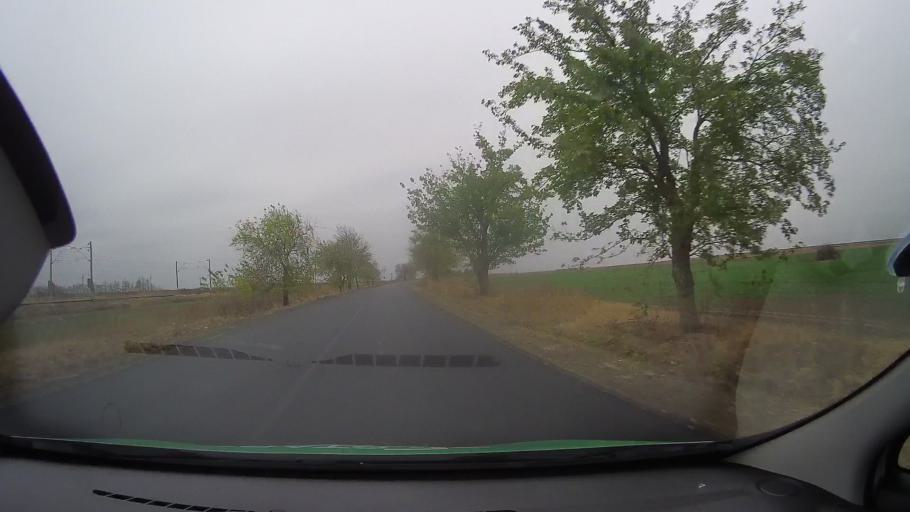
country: RO
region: Ialomita
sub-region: Comuna Valea Ciorii
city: Valea Ciorii
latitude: 44.6982
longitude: 27.5994
